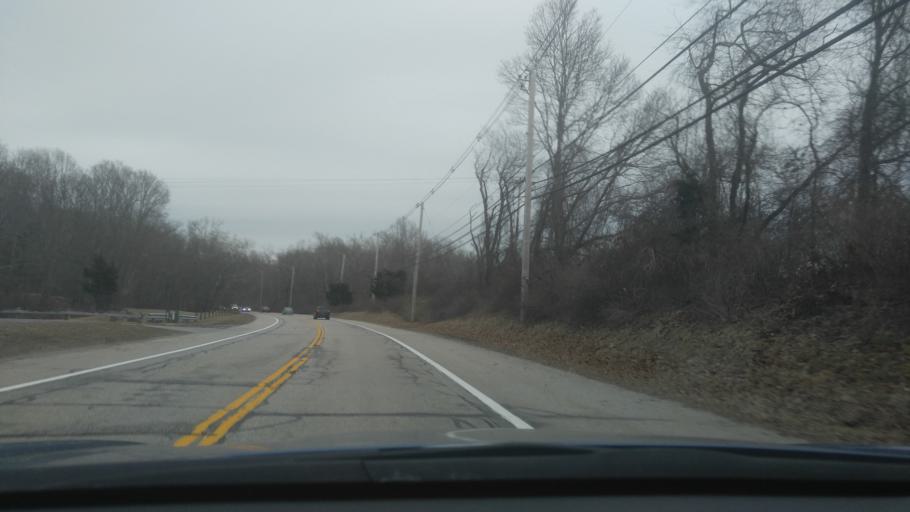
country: US
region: Rhode Island
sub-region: Washington County
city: North Kingstown
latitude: 41.5371
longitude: -71.4377
